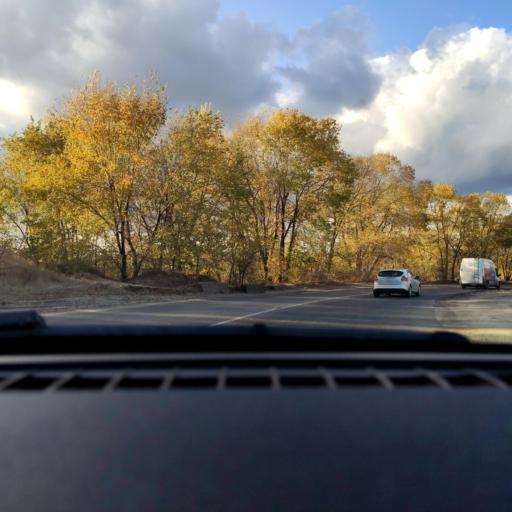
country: RU
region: Voronezj
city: Maslovka
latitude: 51.6206
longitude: 39.2349
